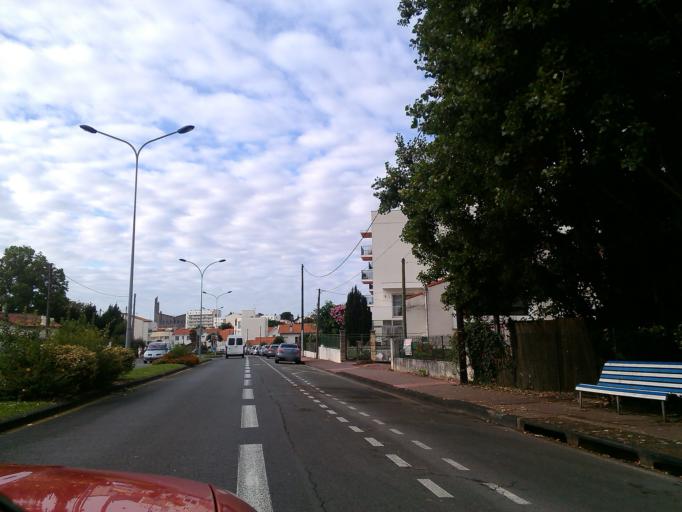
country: FR
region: Poitou-Charentes
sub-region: Departement de la Charente-Maritime
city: Royan
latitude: 45.6309
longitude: -1.0324
